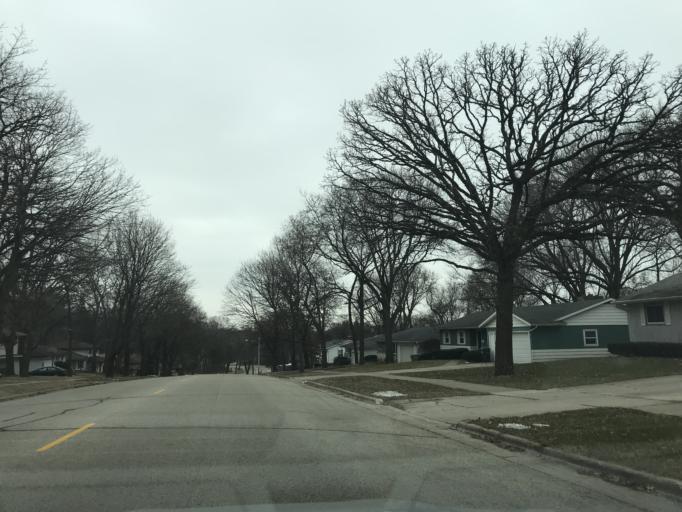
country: US
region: Wisconsin
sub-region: Dane County
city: Monona
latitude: 43.0917
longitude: -89.2974
